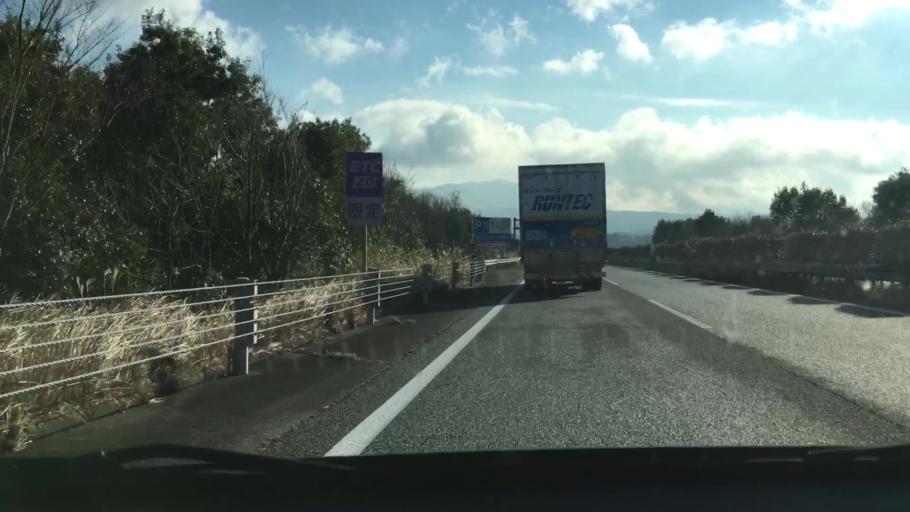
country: JP
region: Kumamoto
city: Hitoyoshi
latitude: 32.0570
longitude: 130.8027
